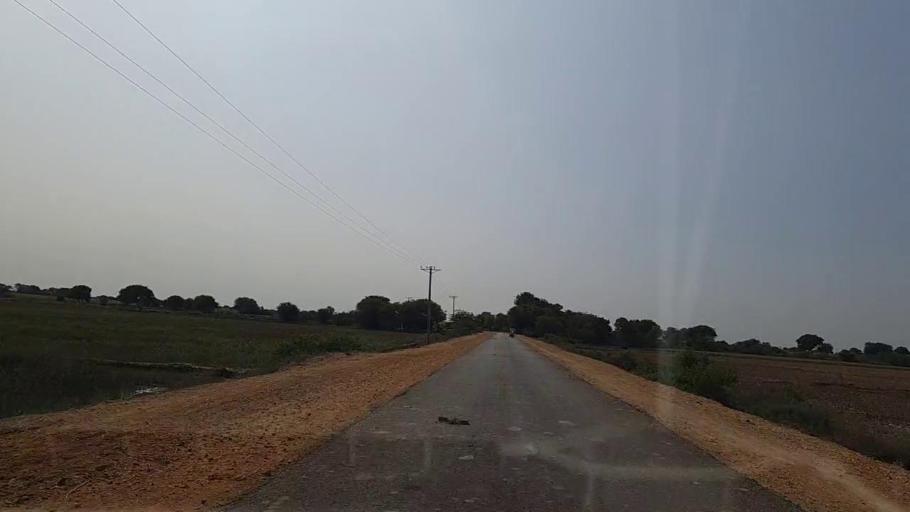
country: PK
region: Sindh
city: Chuhar Jamali
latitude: 24.3483
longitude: 67.9517
